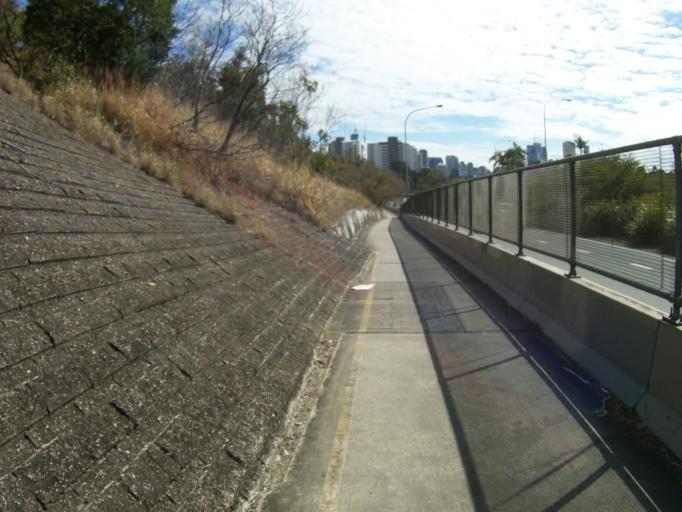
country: AU
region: Queensland
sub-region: Brisbane
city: Woolloongabba
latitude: -27.4879
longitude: 153.0323
